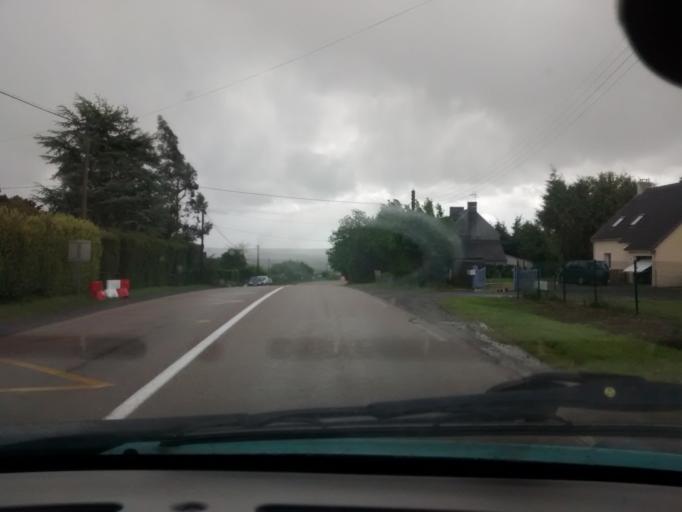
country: FR
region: Lower Normandy
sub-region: Departement de la Manche
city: Conde-sur-Vire
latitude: 49.0778
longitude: -1.0269
